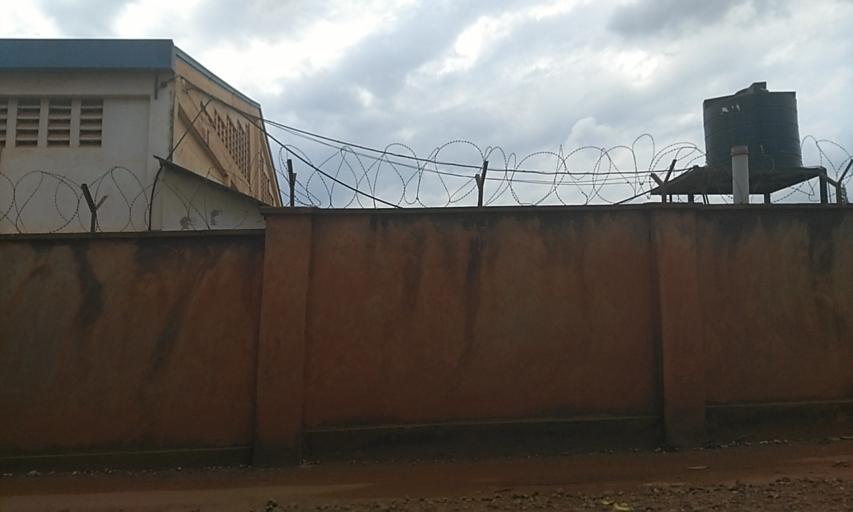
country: UG
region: Central Region
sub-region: Wakiso District
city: Kireka
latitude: 0.3438
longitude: 32.6234
